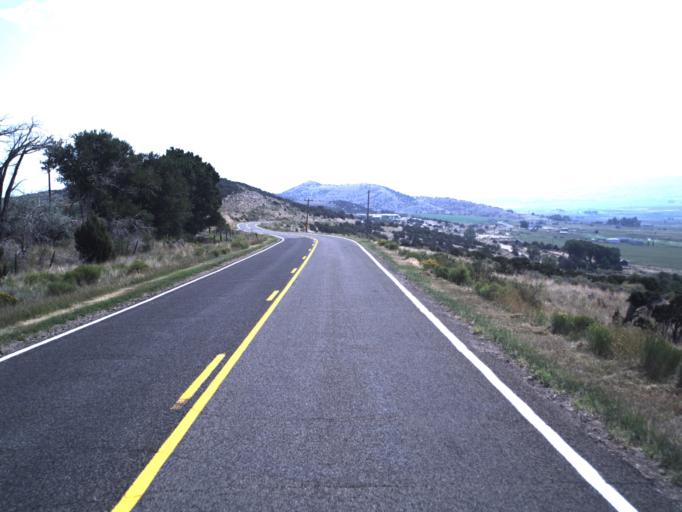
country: US
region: Utah
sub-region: Daggett County
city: Manila
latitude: 40.9784
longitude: -109.7924
